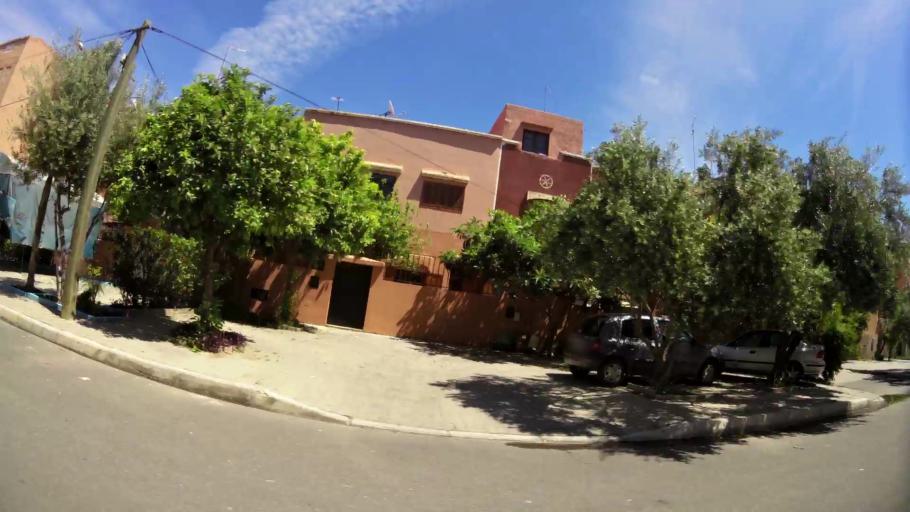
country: MA
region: Marrakech-Tensift-Al Haouz
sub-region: Marrakech
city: Marrakesh
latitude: 31.6424
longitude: -8.0562
